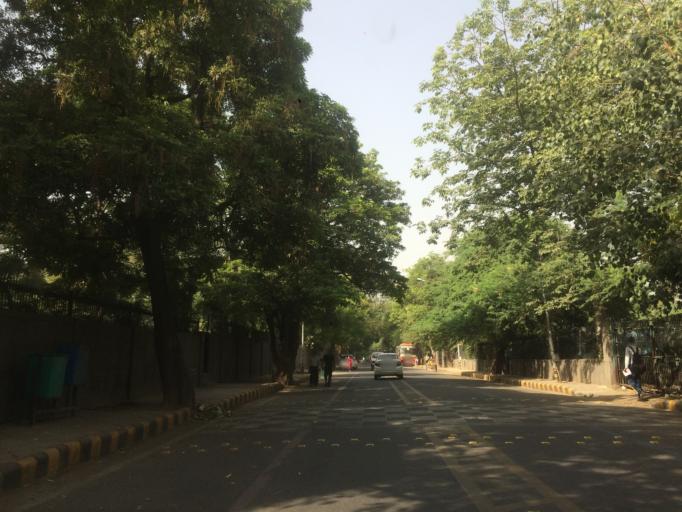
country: IN
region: NCT
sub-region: Central Delhi
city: Karol Bagh
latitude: 28.6324
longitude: 77.2014
